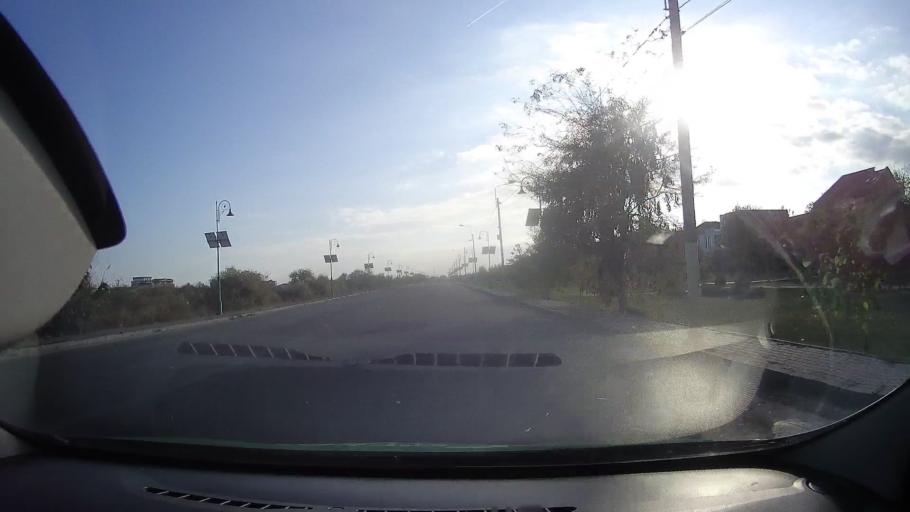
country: RO
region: Constanta
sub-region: Comuna Navodari
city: Navodari
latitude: 44.3126
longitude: 28.6164
